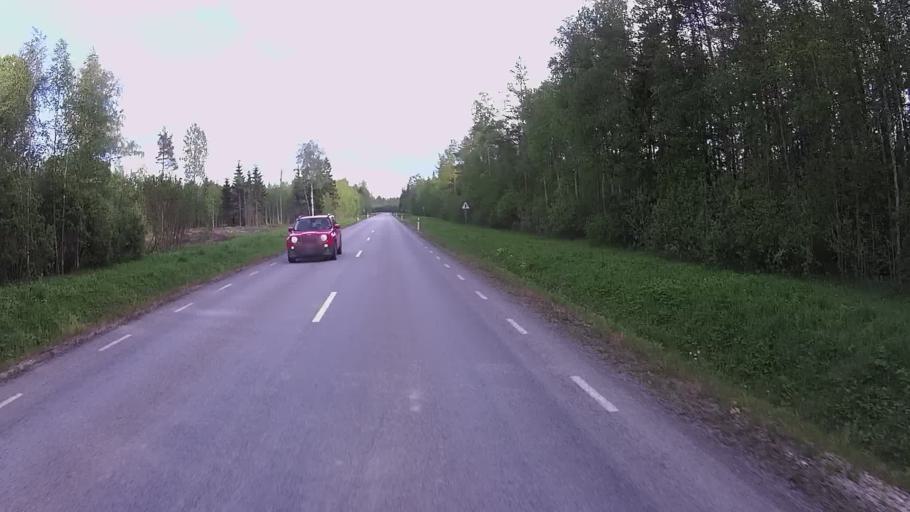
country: EE
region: Jogevamaa
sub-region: Mustvee linn
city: Mustvee
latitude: 59.0669
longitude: 27.0007
